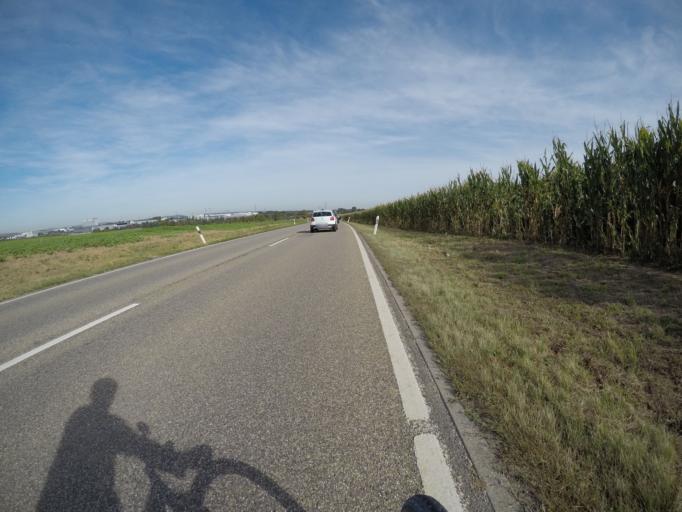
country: DE
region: Baden-Wuerttemberg
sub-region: Regierungsbezirk Stuttgart
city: Schwieberdingen
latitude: 48.8718
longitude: 9.0983
